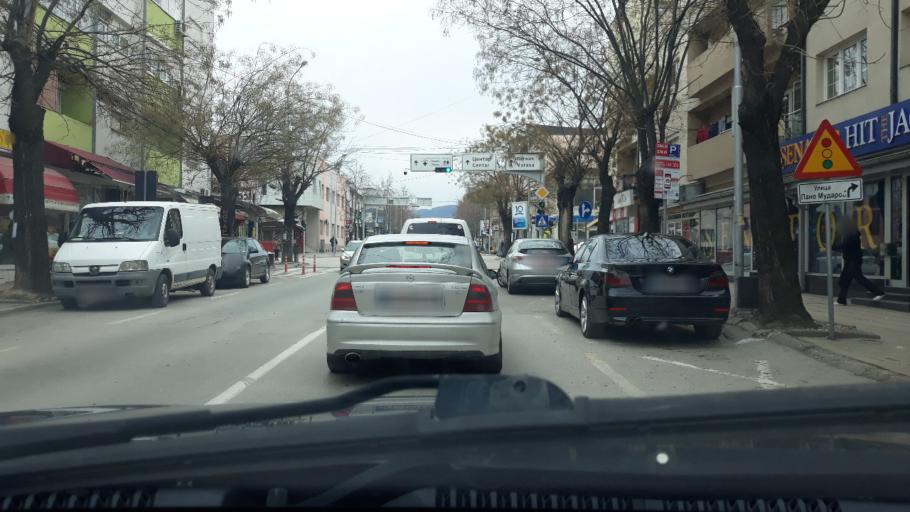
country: MK
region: Kavadarci
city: Kavadarci
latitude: 41.4355
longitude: 22.0113
